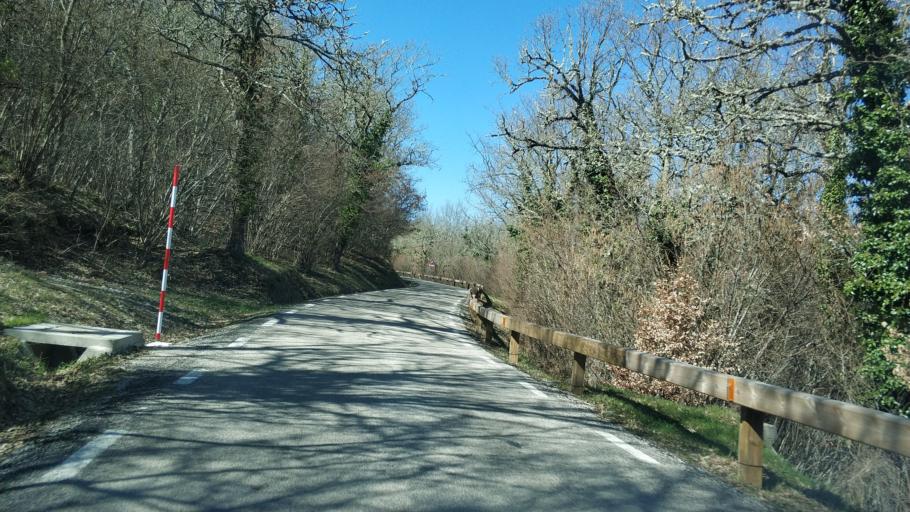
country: ES
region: Cantabria
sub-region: Provincia de Cantabria
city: Mataporquera
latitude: 42.8699
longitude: -4.0710
